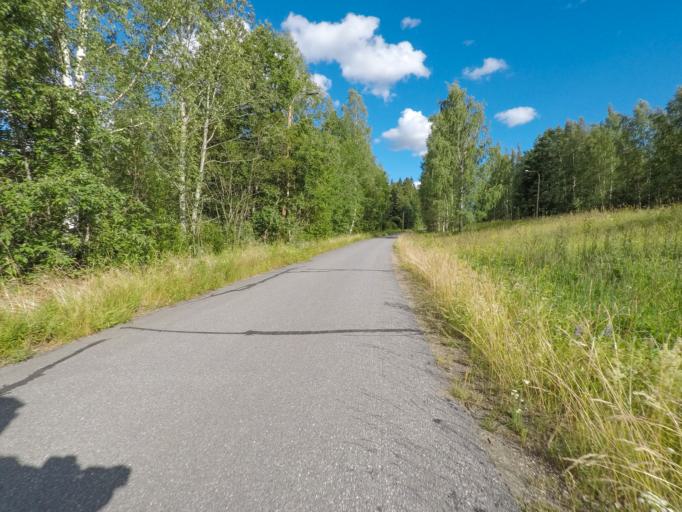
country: FI
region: South Karelia
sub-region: Lappeenranta
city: Taipalsaari
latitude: 61.1056
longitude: 28.1199
